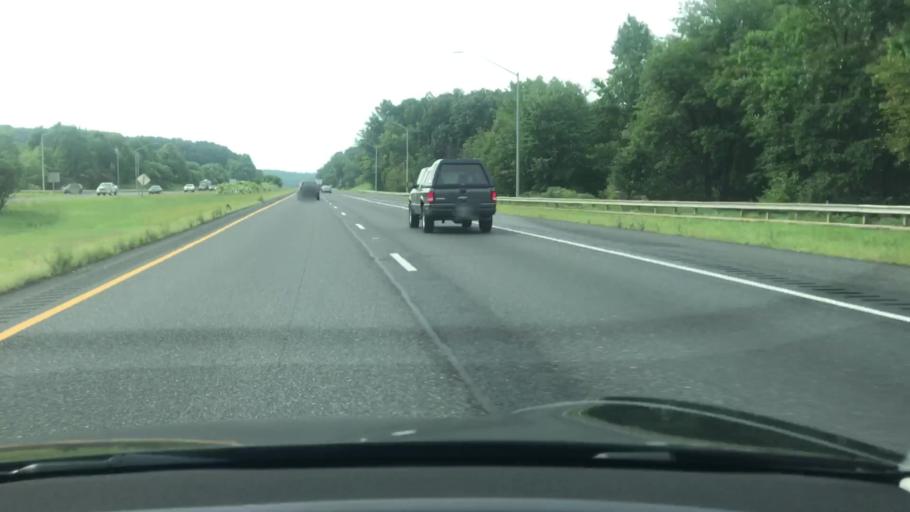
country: US
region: Pennsylvania
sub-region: York County
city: New Freedom
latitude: 39.6306
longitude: -76.6716
